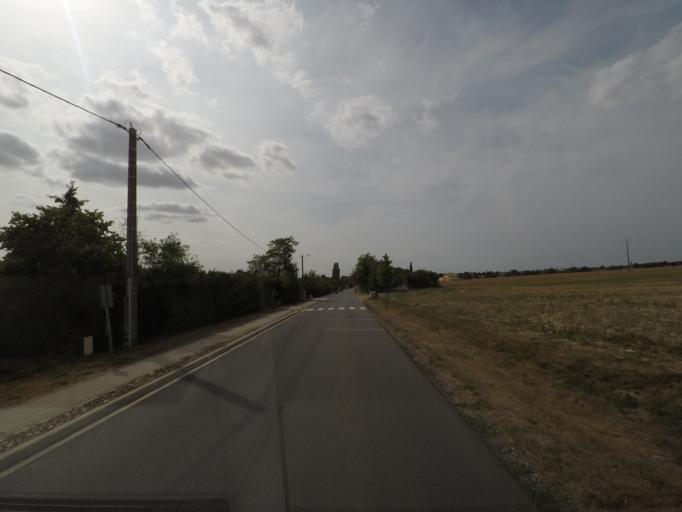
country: FR
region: Poitou-Charentes
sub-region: Departement de la Charente
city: Ruffec
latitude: 46.0257
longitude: 0.2184
